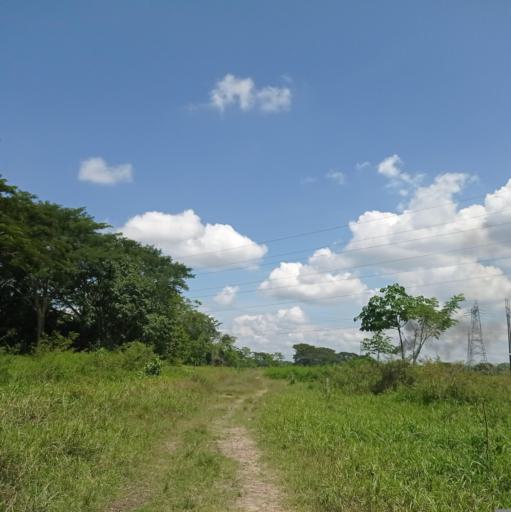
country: CO
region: Santander
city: Barrancabermeja
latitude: 7.0958
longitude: -73.8774
